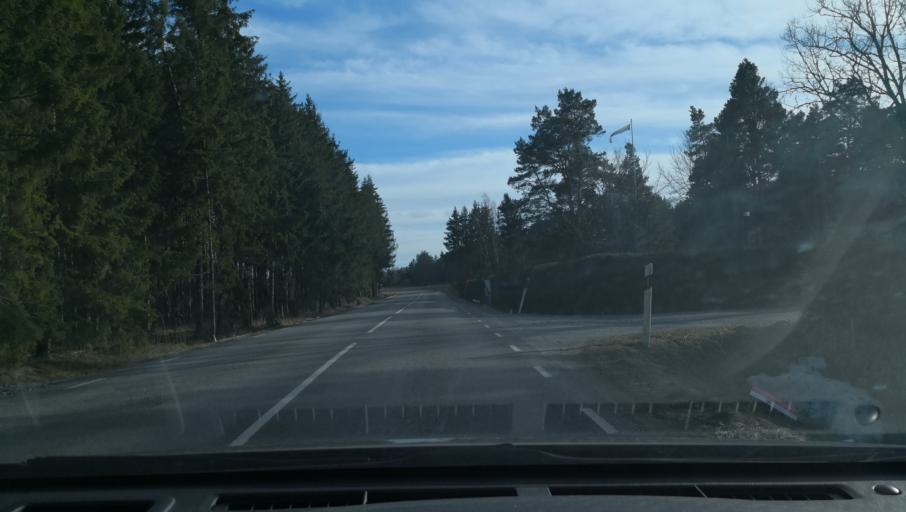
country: SE
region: Uppsala
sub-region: Enkopings Kommun
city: Enkoping
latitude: 59.6194
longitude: 17.0998
